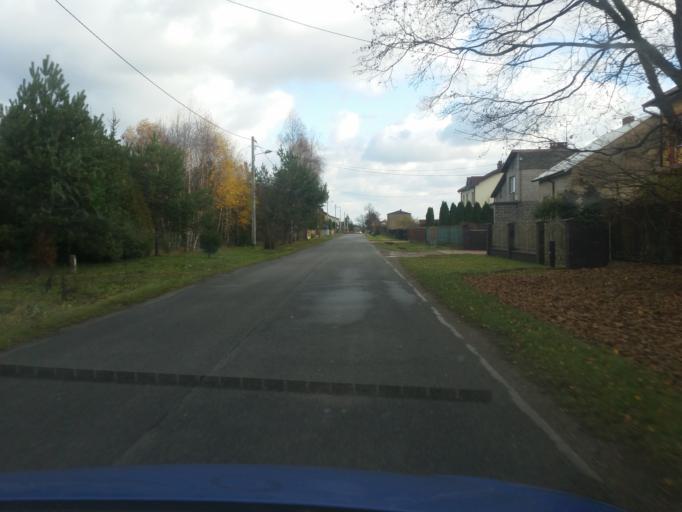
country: PL
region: Silesian Voivodeship
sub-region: Powiat czestochowski
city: Borowno
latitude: 50.9541
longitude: 19.2508
